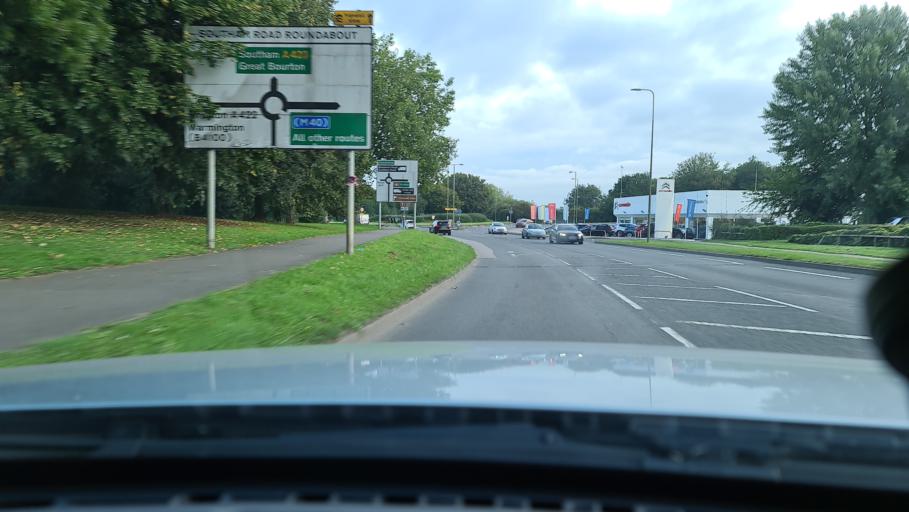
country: GB
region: England
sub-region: Oxfordshire
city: Banbury
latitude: 52.0713
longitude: -1.3379
